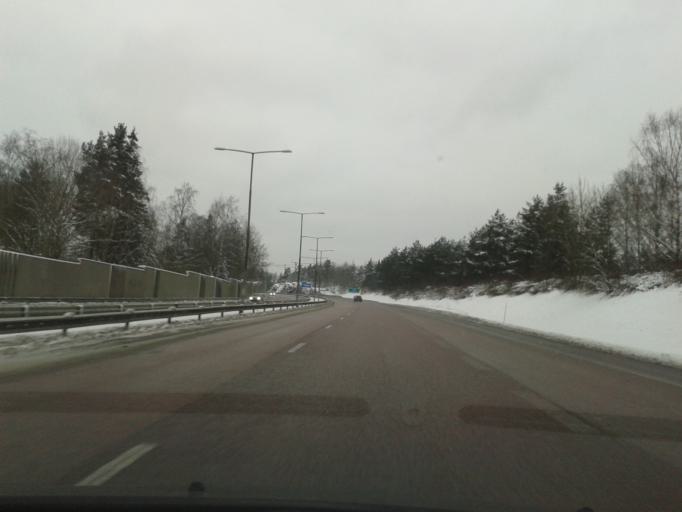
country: SE
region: Stockholm
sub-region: Tyreso Kommun
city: Bollmora
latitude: 59.2497
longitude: 18.2118
